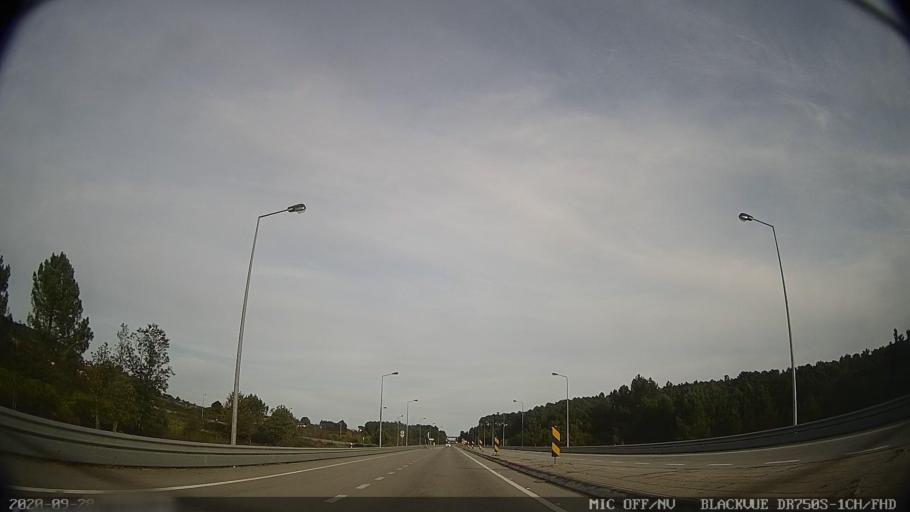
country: PT
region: Vila Real
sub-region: Sabrosa
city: Vilela
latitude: 41.2658
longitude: -7.6387
